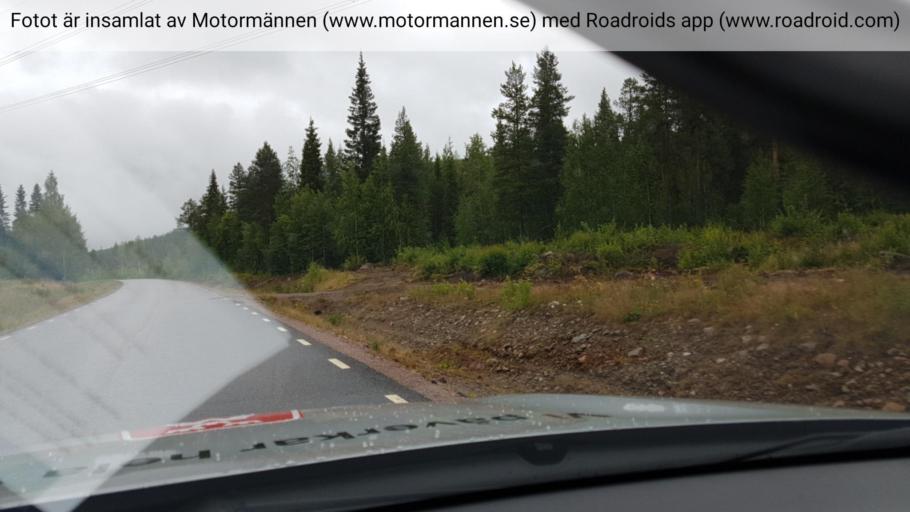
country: SE
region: Norrbotten
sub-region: Gallivare Kommun
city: Gaellivare
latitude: 66.6613
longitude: 20.3744
